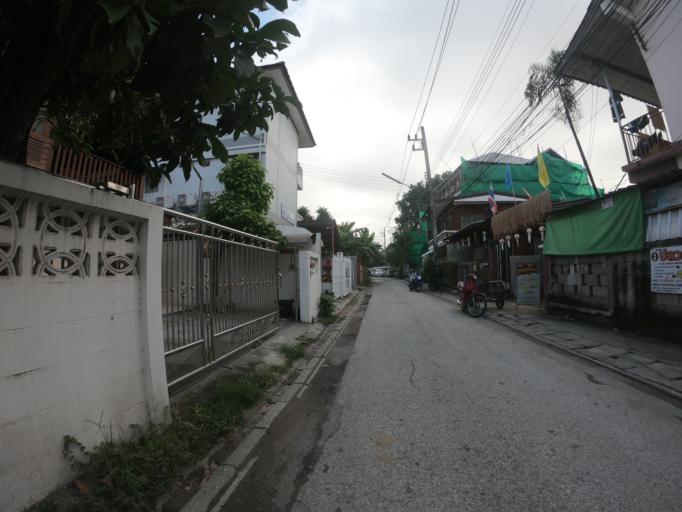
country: TH
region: Chiang Mai
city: Chiang Mai
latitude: 18.7935
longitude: 98.9796
